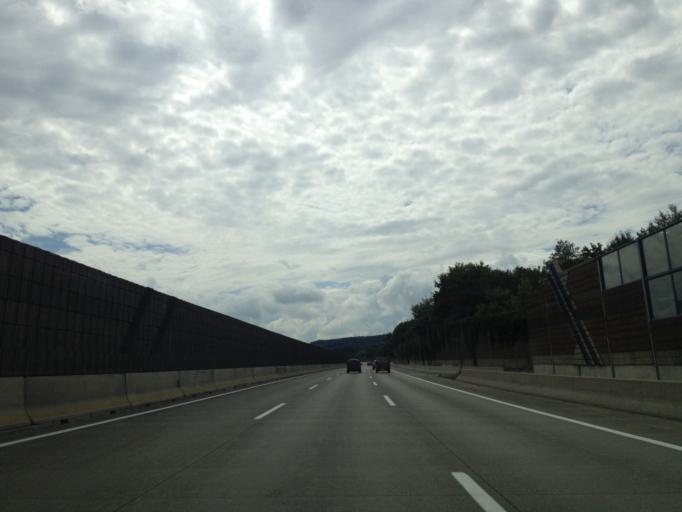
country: AT
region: Styria
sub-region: Politischer Bezirk Weiz
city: Ungerdorf
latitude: 47.0902
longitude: 15.6713
